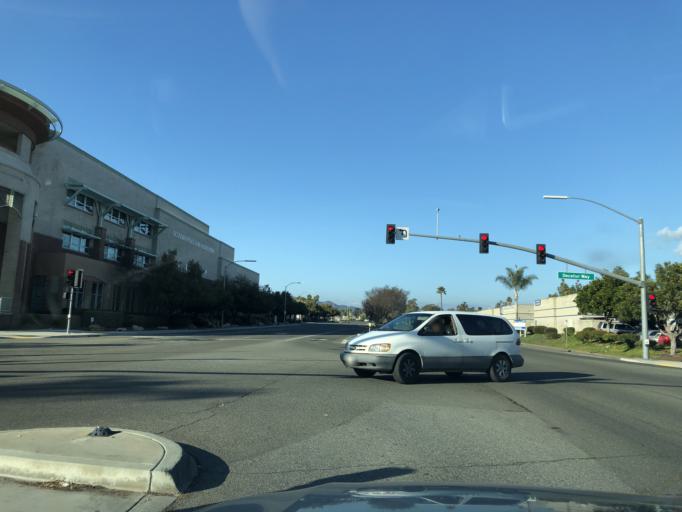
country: US
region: California
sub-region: San Diego County
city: Escondido
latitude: 33.1353
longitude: -117.0934
